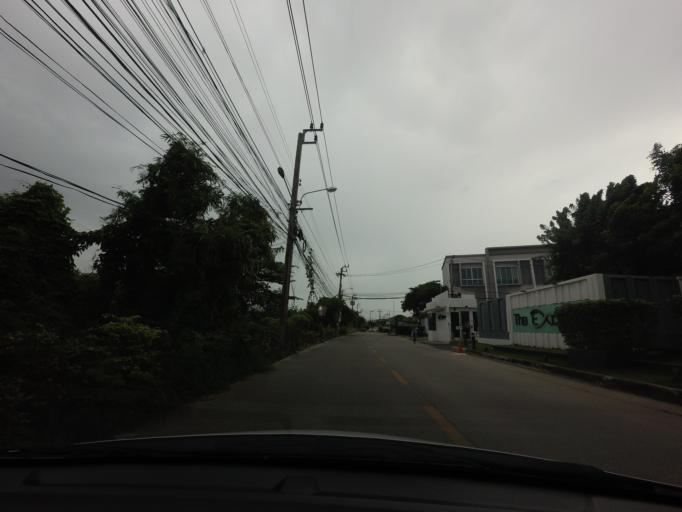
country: TH
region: Bangkok
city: Suan Luang
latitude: 13.7308
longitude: 100.6329
